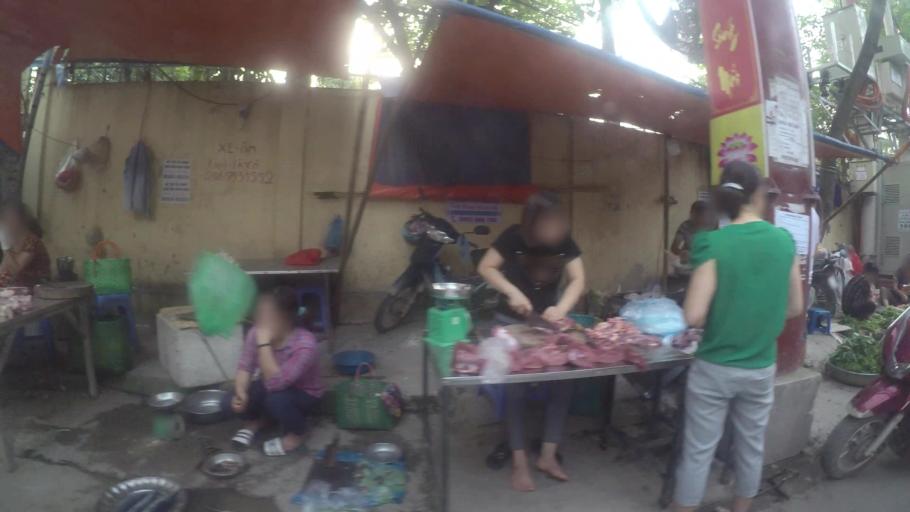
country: VN
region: Ha Noi
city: Ha Dong
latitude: 20.9939
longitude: 105.7296
